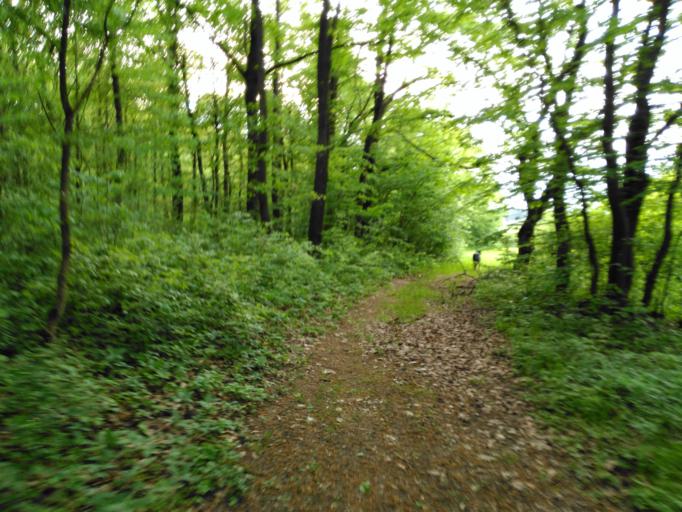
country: CZ
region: Central Bohemia
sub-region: Okres Beroun
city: Beroun
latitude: 49.9130
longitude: 14.0791
